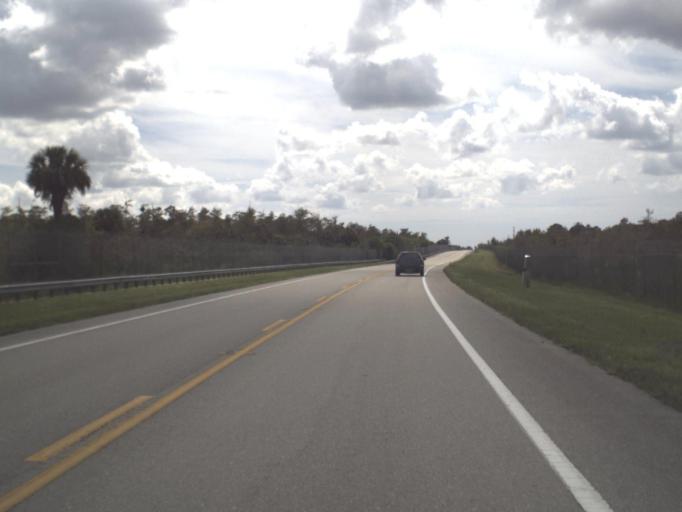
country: US
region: Florida
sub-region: Collier County
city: Lely Resort
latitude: 25.9867
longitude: -81.3478
